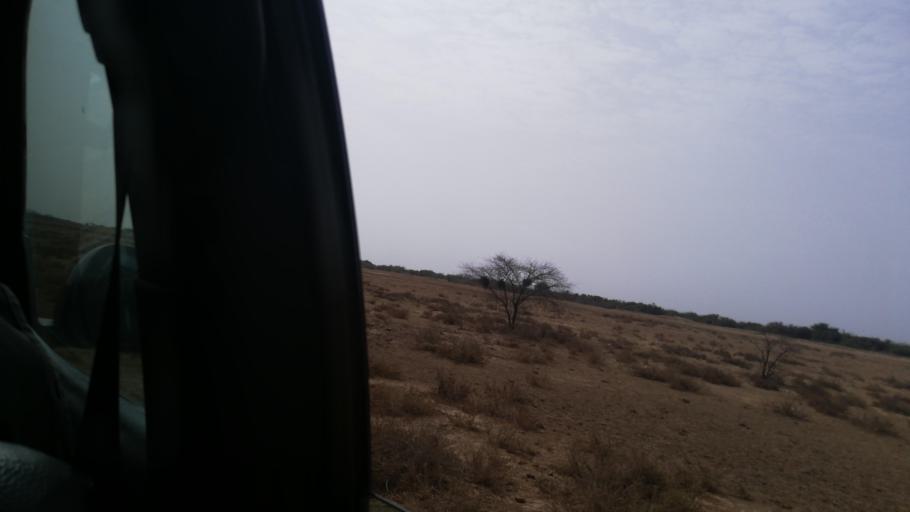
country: SN
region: Saint-Louis
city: Rosso
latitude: 16.3736
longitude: -16.1949
